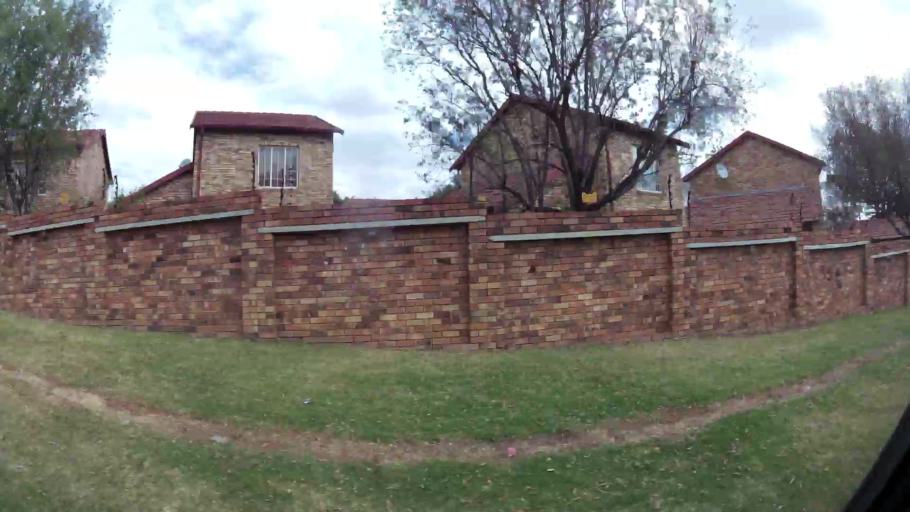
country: ZA
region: Gauteng
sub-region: City of Johannesburg Metropolitan Municipality
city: Roodepoort
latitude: -26.1013
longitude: 27.8997
